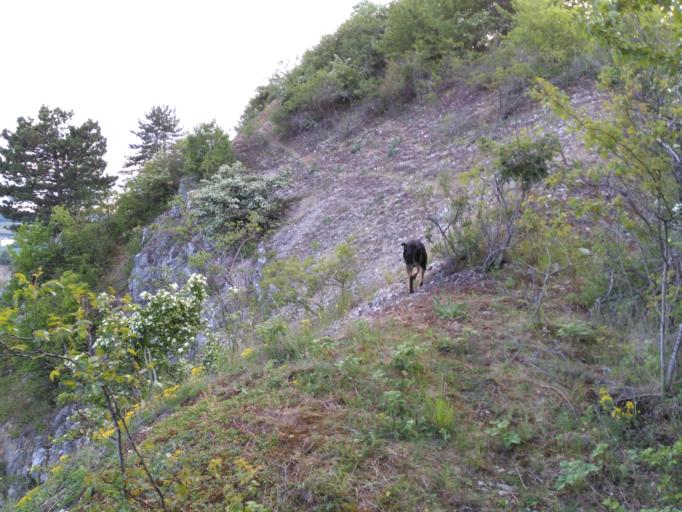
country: CZ
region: Central Bohemia
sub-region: Okres Beroun
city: Kraluv Dvur
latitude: 49.9183
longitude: 14.0599
